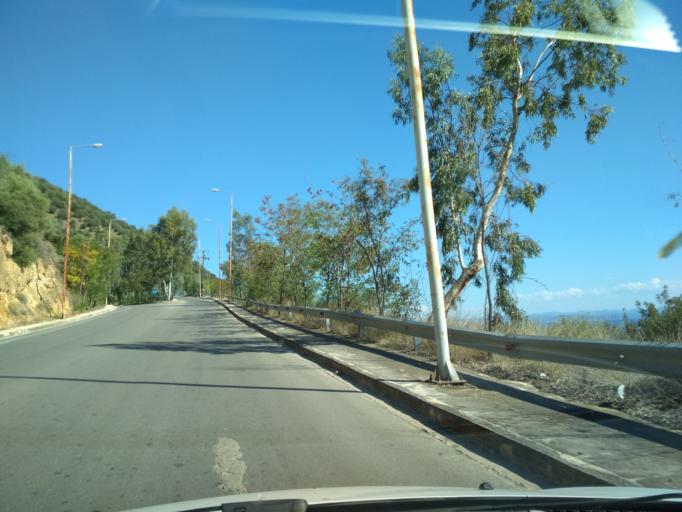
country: GR
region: Central Greece
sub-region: Nomos Evvoias
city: Oreoi
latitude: 38.8526
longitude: 23.0539
